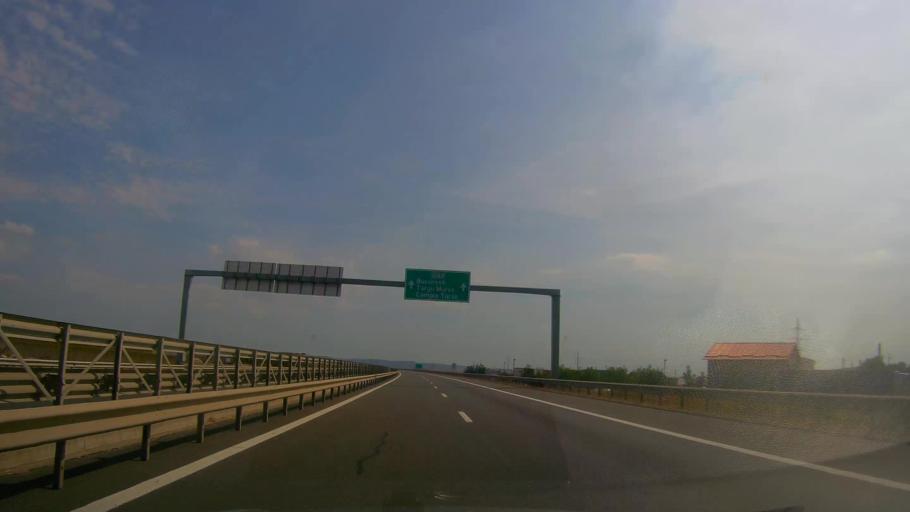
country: RO
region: Cluj
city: Turda
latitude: 46.5238
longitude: 23.8056
